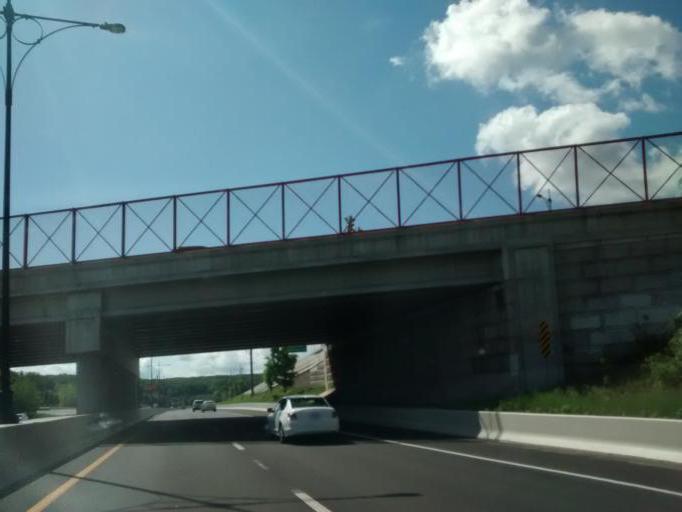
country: US
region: Massachusetts
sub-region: Worcester County
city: Sunderland
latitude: 42.2365
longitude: -71.7939
